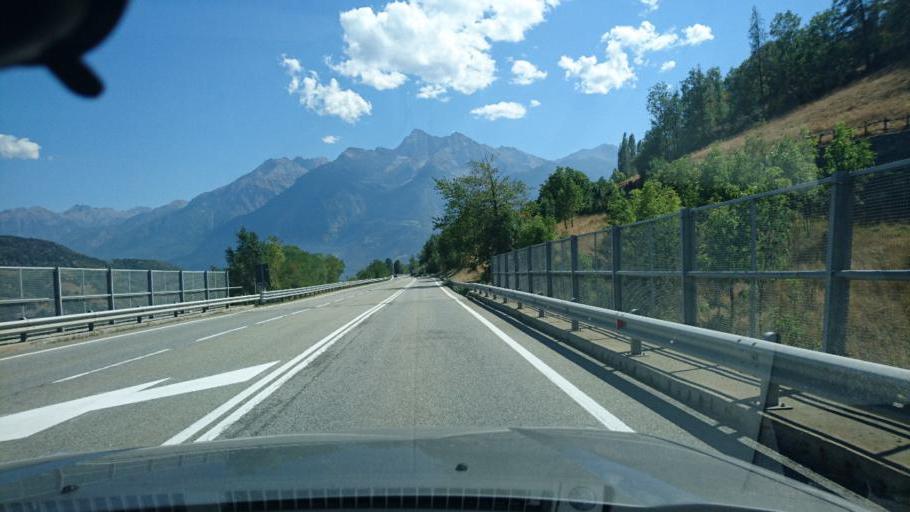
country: IT
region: Aosta Valley
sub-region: Valle d'Aosta
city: Gignod
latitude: 45.7726
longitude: 7.3013
